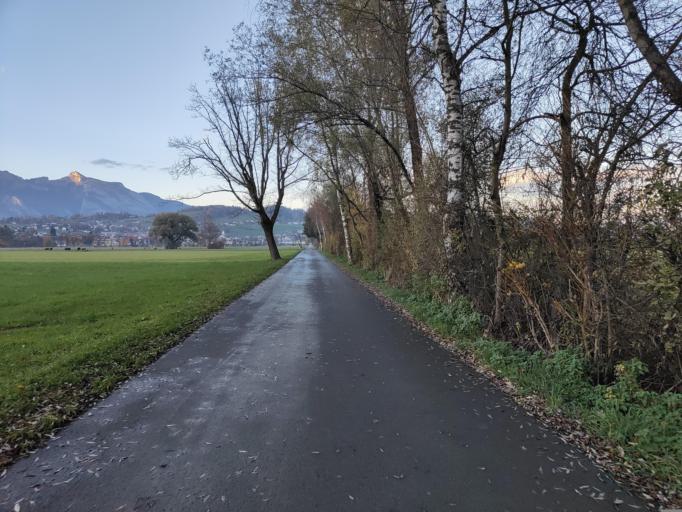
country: LI
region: Eschen
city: Eschen
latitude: 47.1981
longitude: 9.5252
